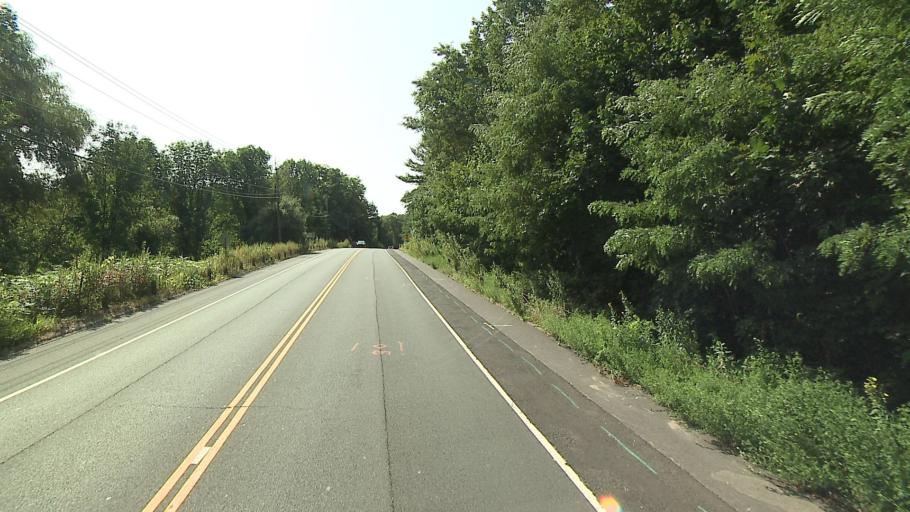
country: US
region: Connecticut
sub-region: Fairfield County
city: Newtown
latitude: 41.4211
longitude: -73.3551
